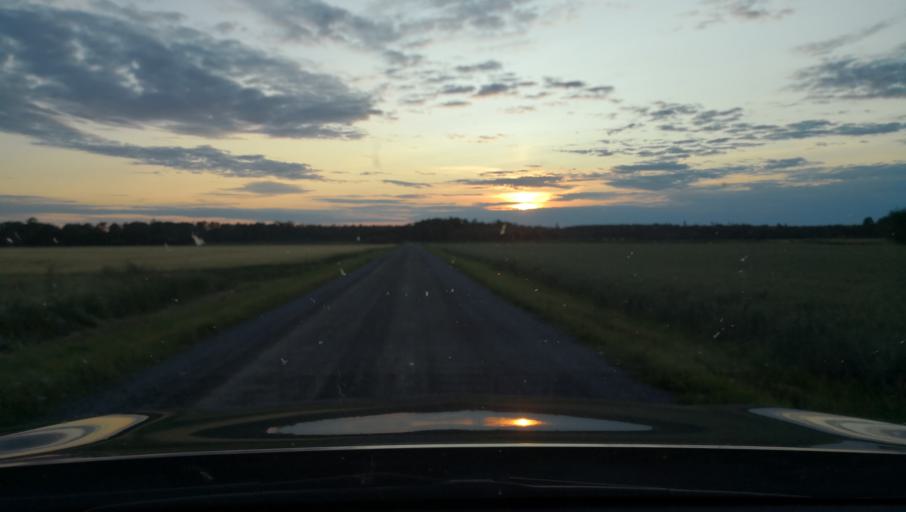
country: SE
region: Uppsala
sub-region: Osthammars Kommun
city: Bjorklinge
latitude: 60.0577
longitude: 17.5898
